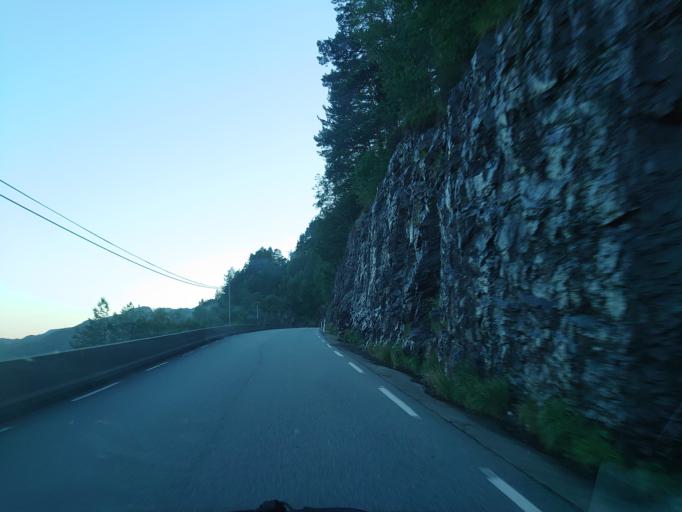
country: NO
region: Hordaland
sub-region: Osteroy
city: Lonevag
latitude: 60.7084
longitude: 5.6110
